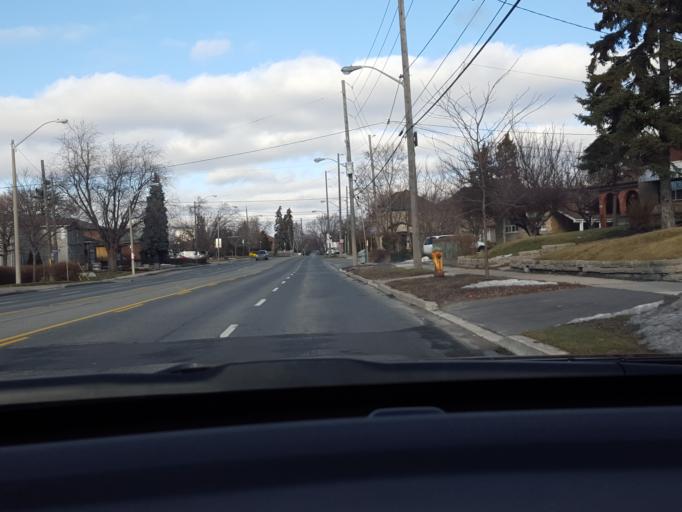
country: CA
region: Ontario
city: Etobicoke
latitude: 43.7223
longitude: -79.5371
